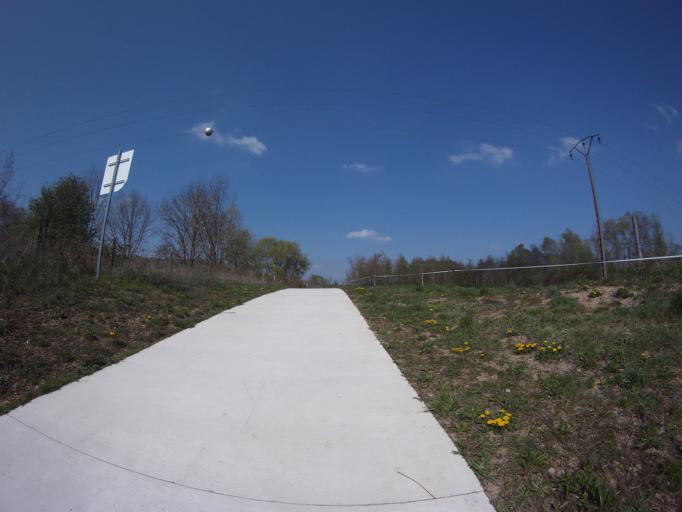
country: FR
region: Lorraine
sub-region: Departement de Meurthe-et-Moselle
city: Dieulouard
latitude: 48.8466
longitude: 6.0802
